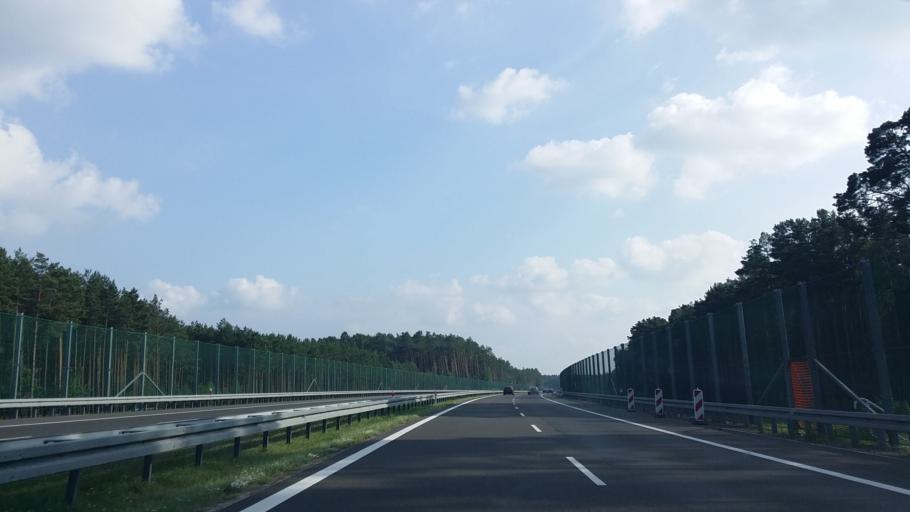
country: PL
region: Lubusz
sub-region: Powiat miedzyrzecki
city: Miedzyrzecz
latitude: 52.4999
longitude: 15.5542
